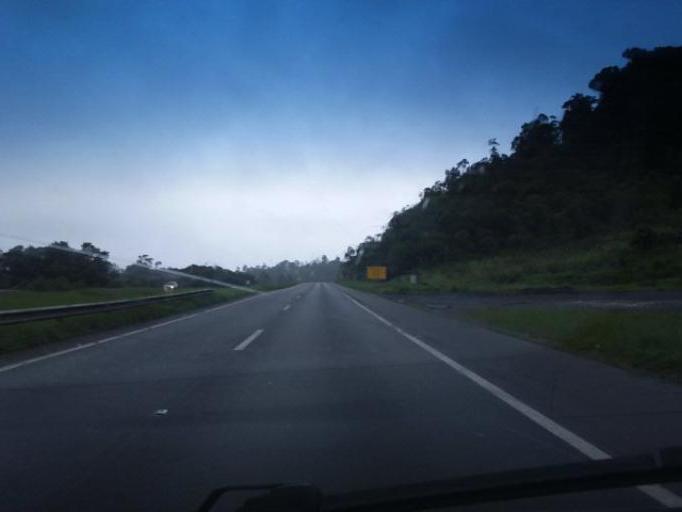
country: BR
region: Sao Paulo
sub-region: Cajati
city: Cajati
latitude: -25.0026
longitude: -48.5083
